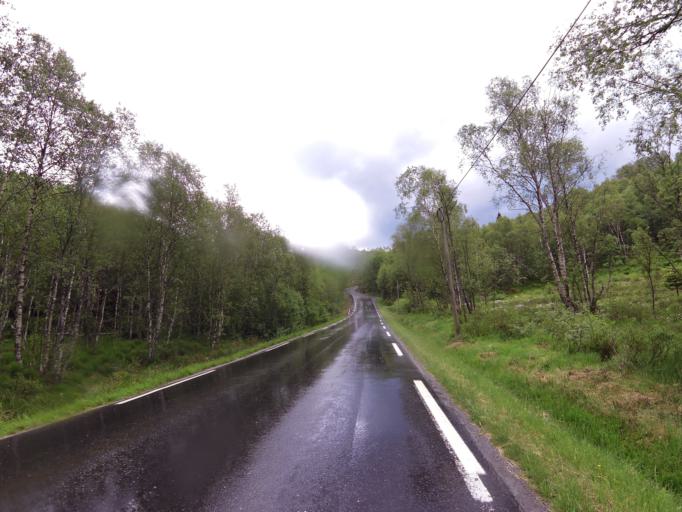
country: NO
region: Vest-Agder
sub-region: Lyngdal
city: Lyngdal
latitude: 58.1091
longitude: 7.0898
